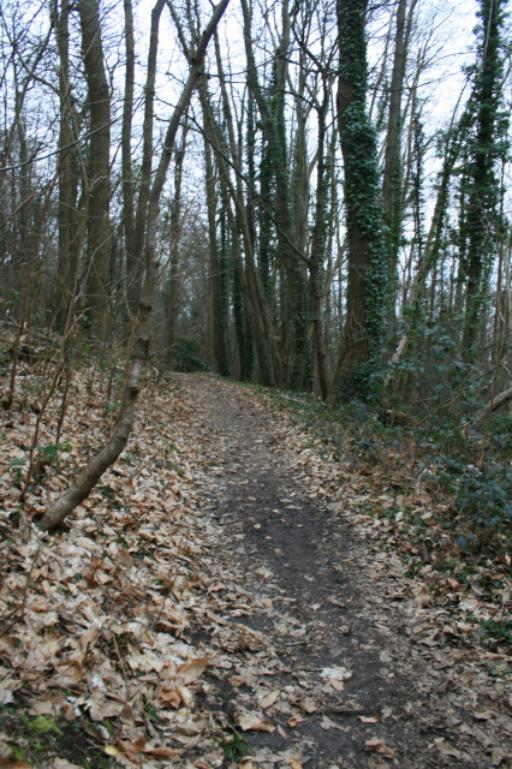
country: FR
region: Ile-de-France
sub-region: Departement des Yvelines
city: Triel-sur-Seine
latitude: 48.9929
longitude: 1.9994
